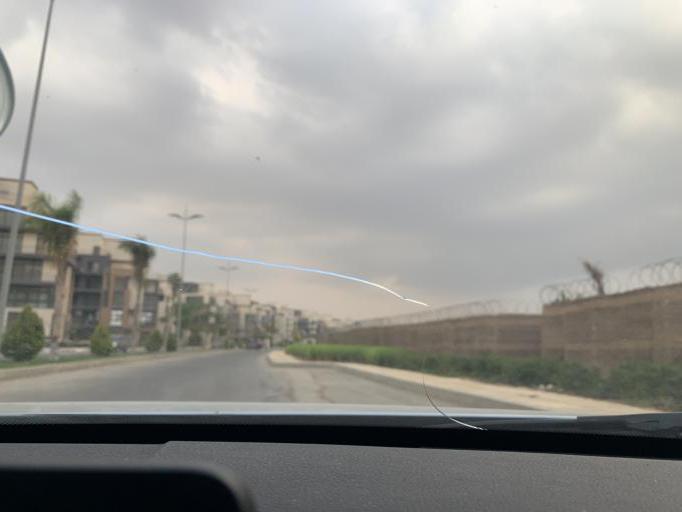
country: EG
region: Muhafazat al Qalyubiyah
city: Al Khankah
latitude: 30.0993
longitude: 31.6589
